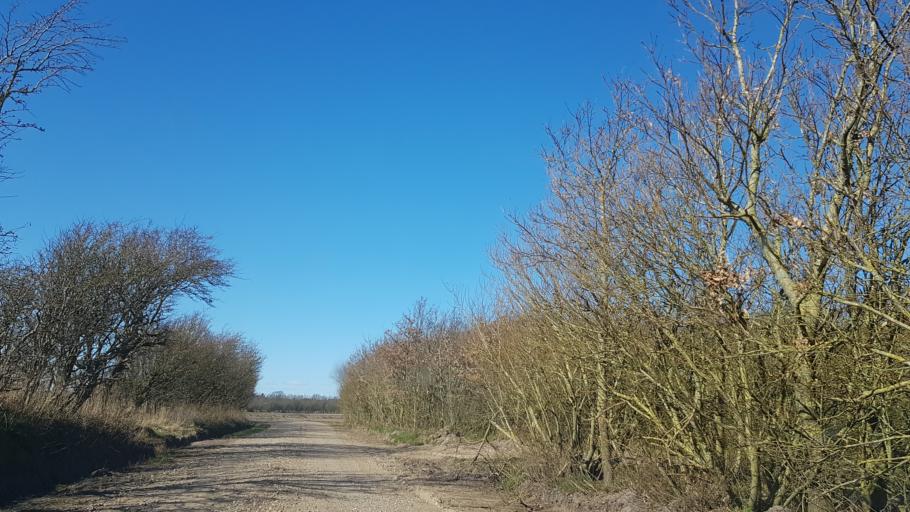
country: DK
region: South Denmark
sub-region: Esbjerg Kommune
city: Ribe
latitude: 55.2485
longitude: 8.7100
